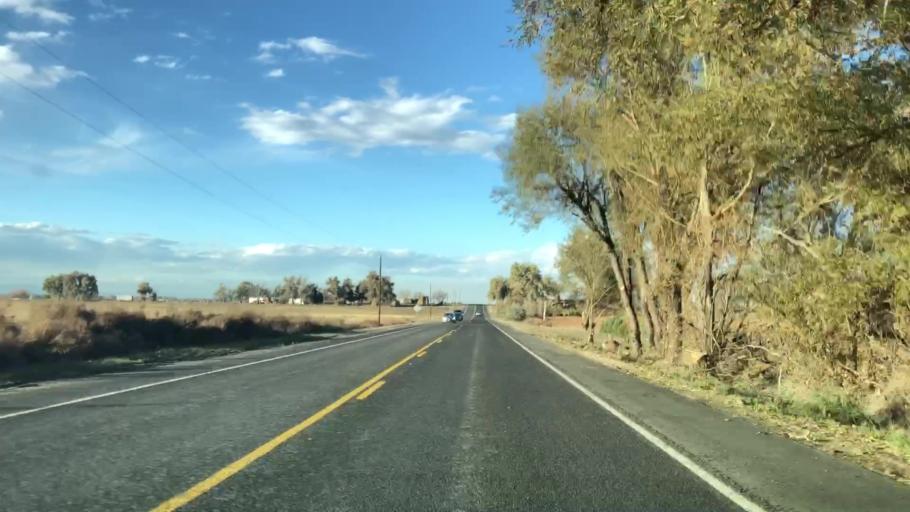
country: US
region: Colorado
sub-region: Larimer County
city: Loveland
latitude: 40.4682
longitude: -105.0203
